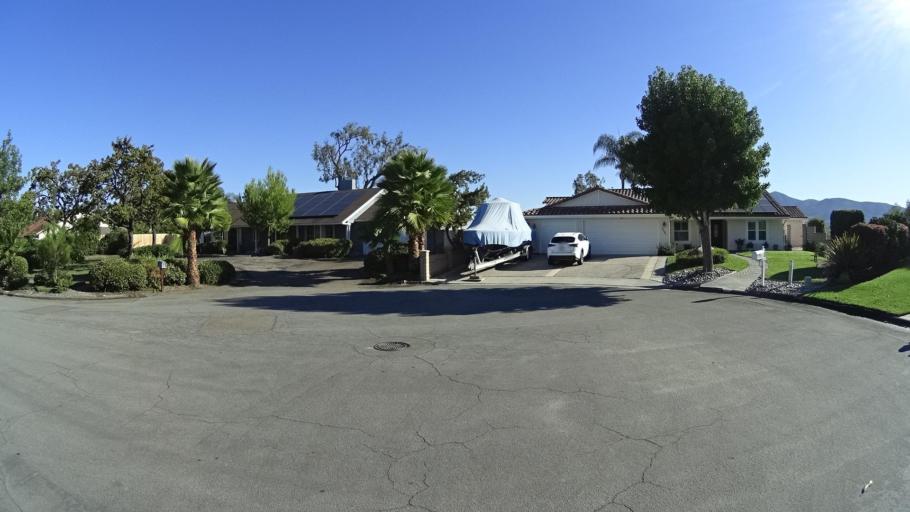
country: US
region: California
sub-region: San Diego County
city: Bonita
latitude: 32.6847
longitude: -117.0222
